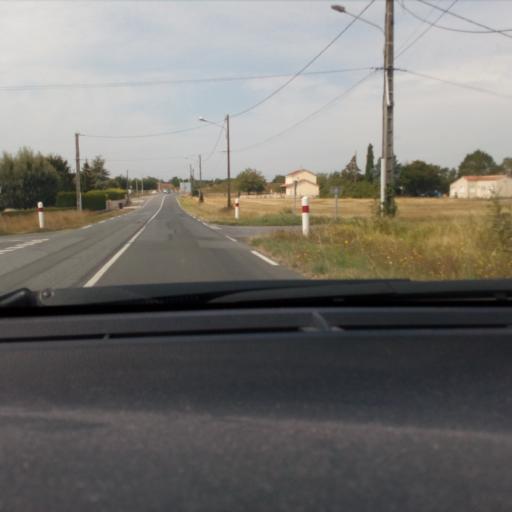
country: FR
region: Poitou-Charentes
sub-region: Departement de la Charente
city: Saint-Yrieix-sur-Charente
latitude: 45.6857
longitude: 0.1105
